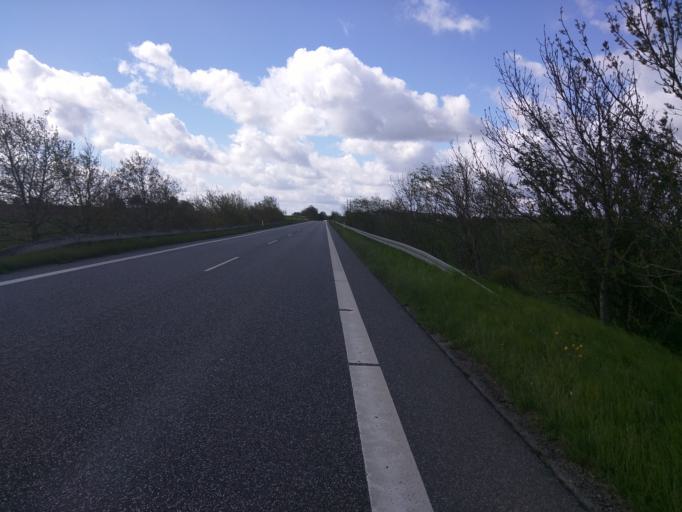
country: DK
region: Central Jutland
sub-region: Silkeborg Kommune
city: Kjellerup
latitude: 56.3526
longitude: 9.4347
